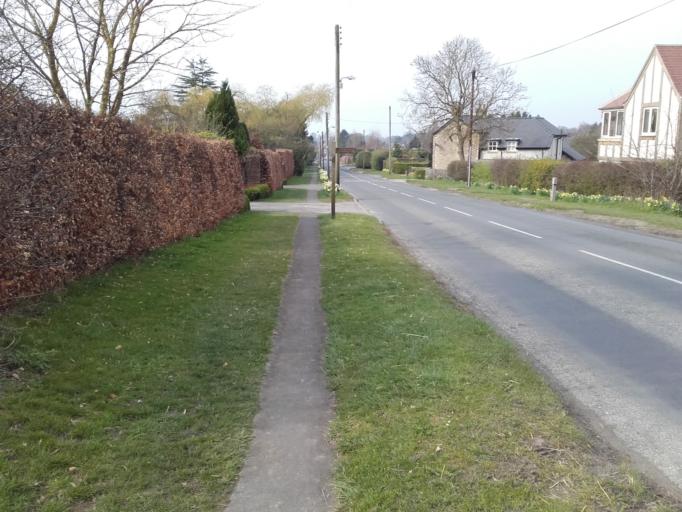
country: GB
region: England
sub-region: East Riding of Yorkshire
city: South Cave
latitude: 53.7733
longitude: -0.5895
